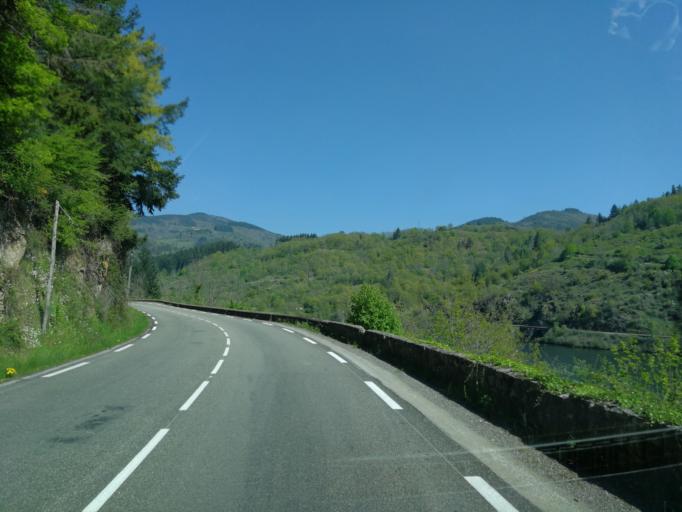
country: FR
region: Rhone-Alpes
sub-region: Departement de l'Ardeche
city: Le Cheylard
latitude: 44.9073
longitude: 4.4688
